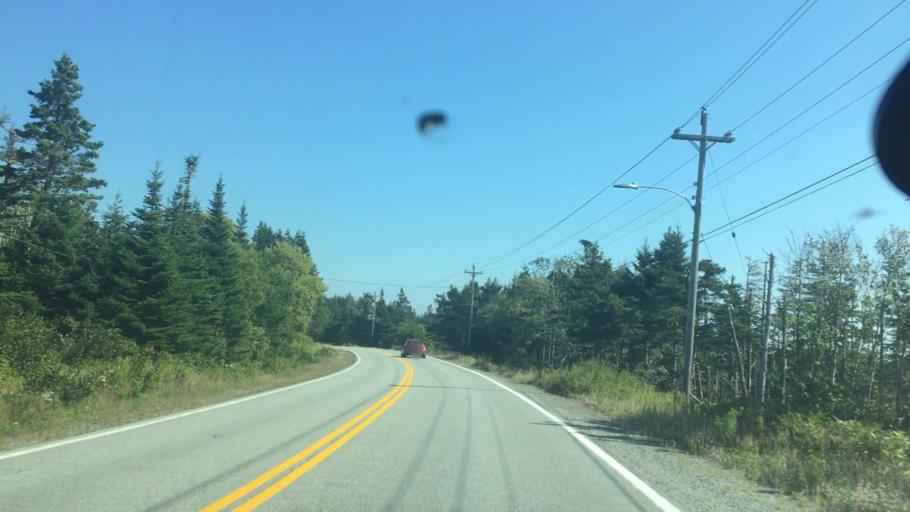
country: CA
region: Nova Scotia
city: Antigonish
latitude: 44.9346
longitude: -62.2729
